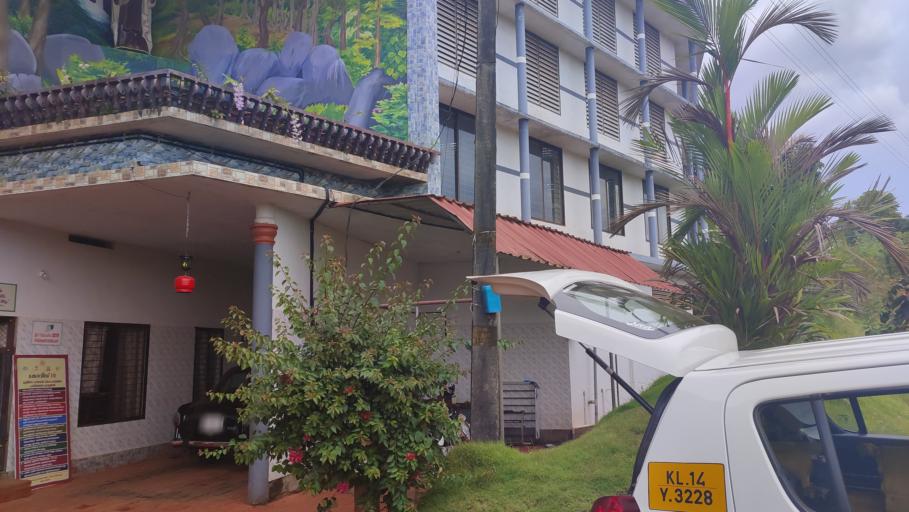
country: IN
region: Karnataka
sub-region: Dakshina Kannada
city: Sulya
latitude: 12.4460
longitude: 75.2451
